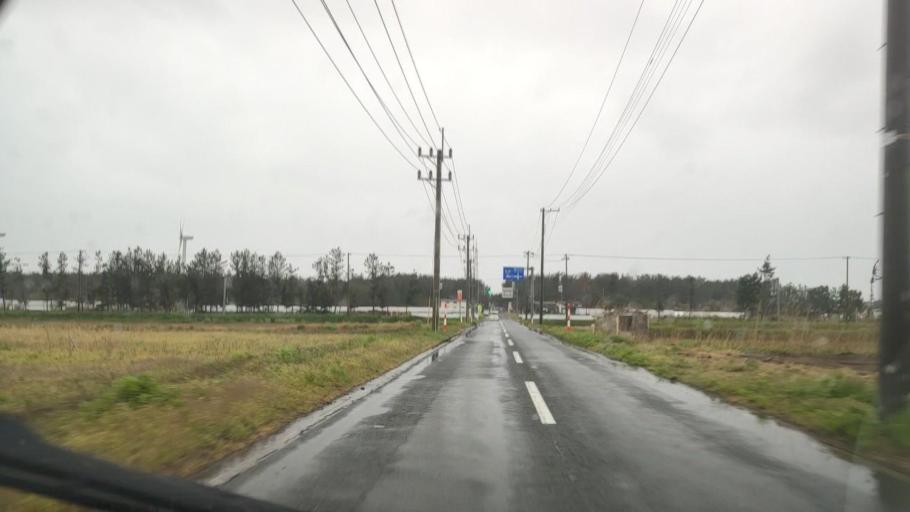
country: JP
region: Akita
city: Noshiromachi
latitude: 40.0973
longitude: 139.9684
